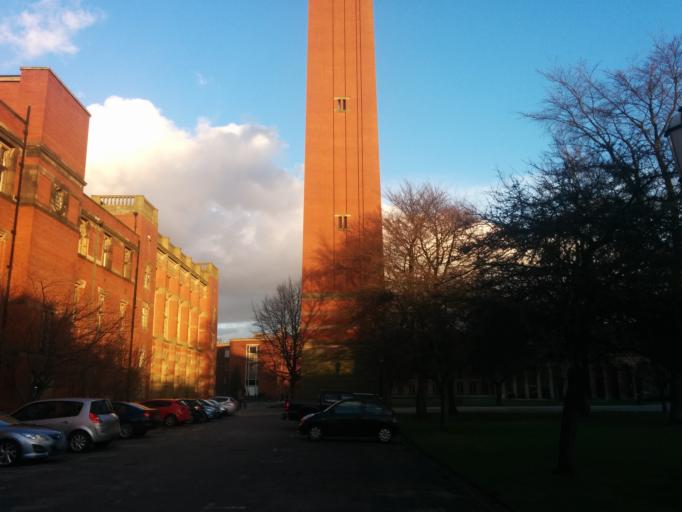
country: GB
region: England
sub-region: City and Borough of Birmingham
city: Birmingham
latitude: 52.4500
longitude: -1.9316
